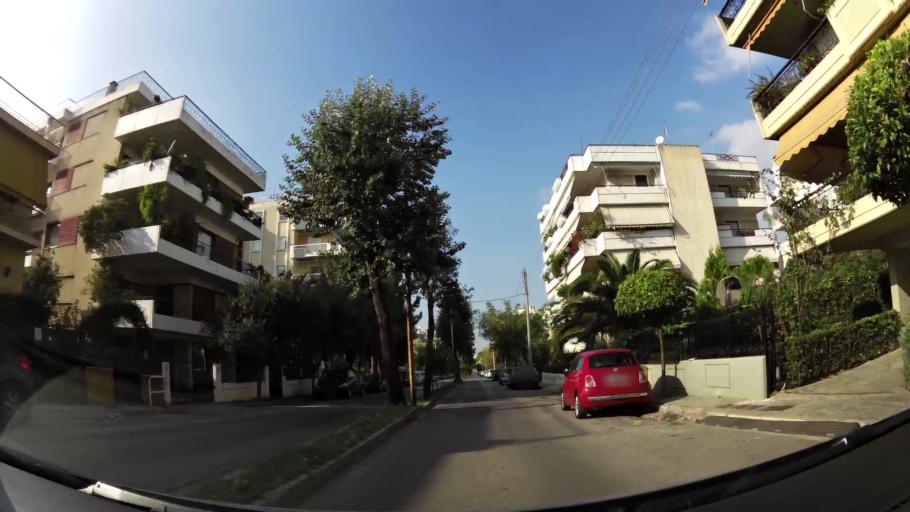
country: GR
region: Attica
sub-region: Nomarchia Athinas
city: Cholargos
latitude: 38.0059
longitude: 23.8072
